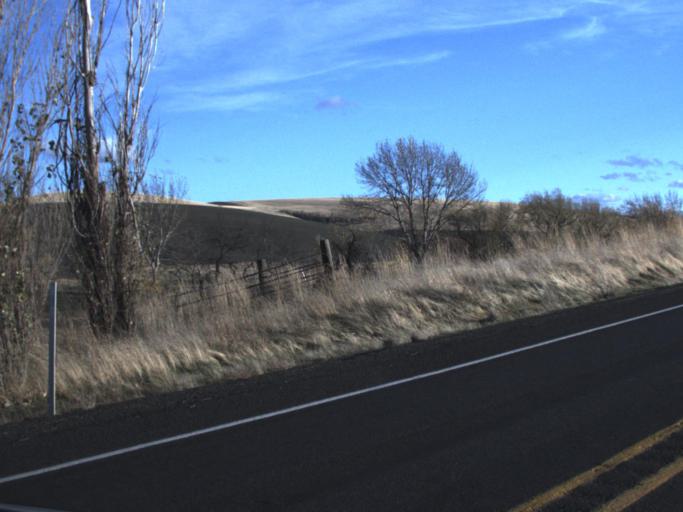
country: US
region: Washington
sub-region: Walla Walla County
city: Waitsburg
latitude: 46.2586
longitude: -118.1528
